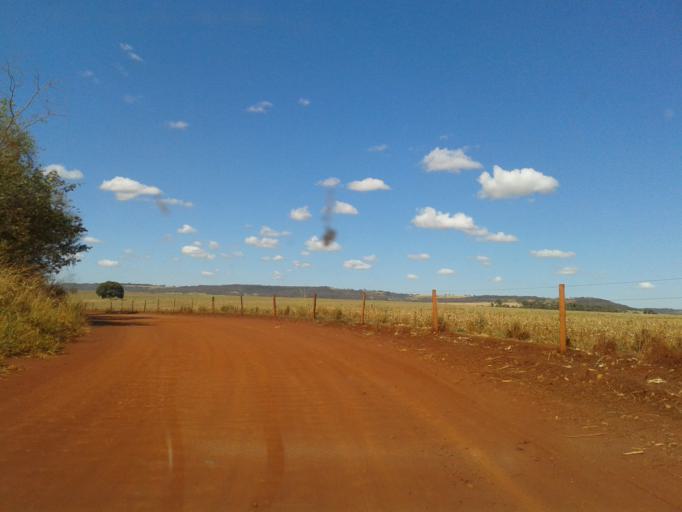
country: BR
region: Minas Gerais
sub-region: Centralina
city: Centralina
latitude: -18.5724
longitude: -49.1363
